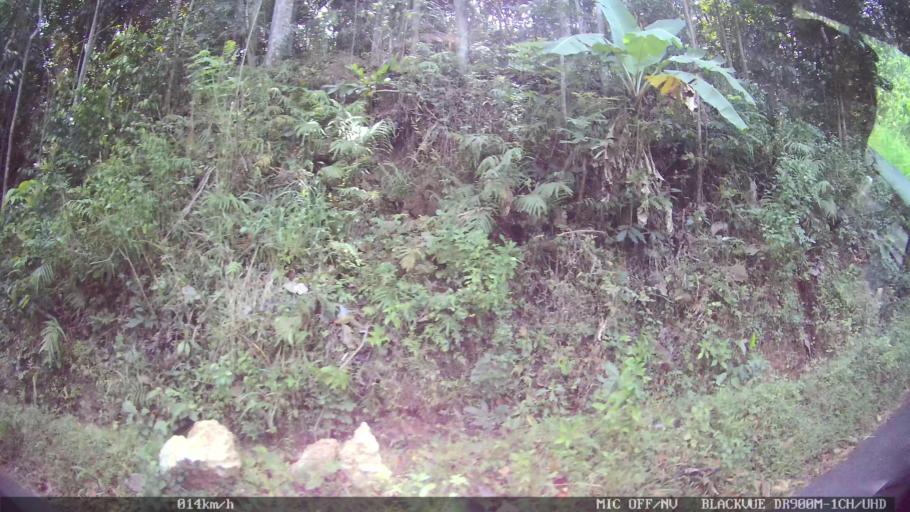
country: ID
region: Central Java
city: Candi Prambanan
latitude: -7.8165
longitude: 110.5157
